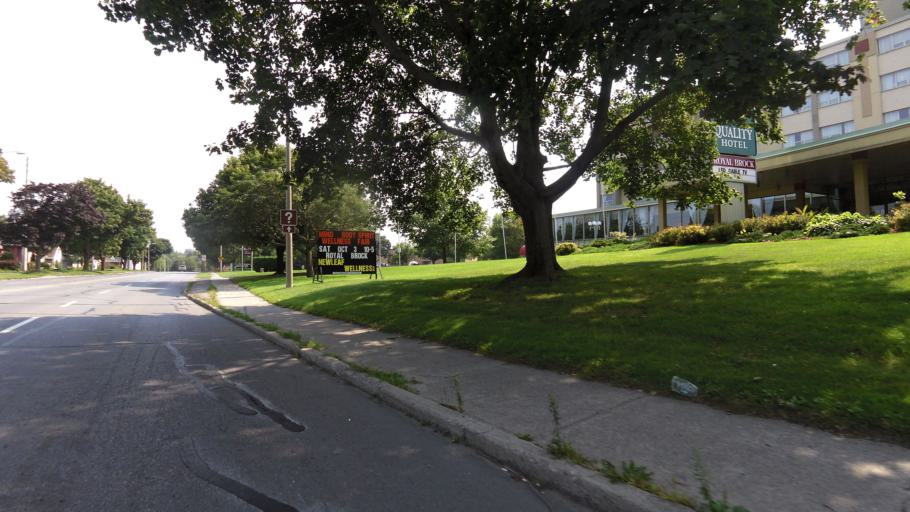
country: CA
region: Ontario
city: Brockville
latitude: 44.5976
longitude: -75.6961
